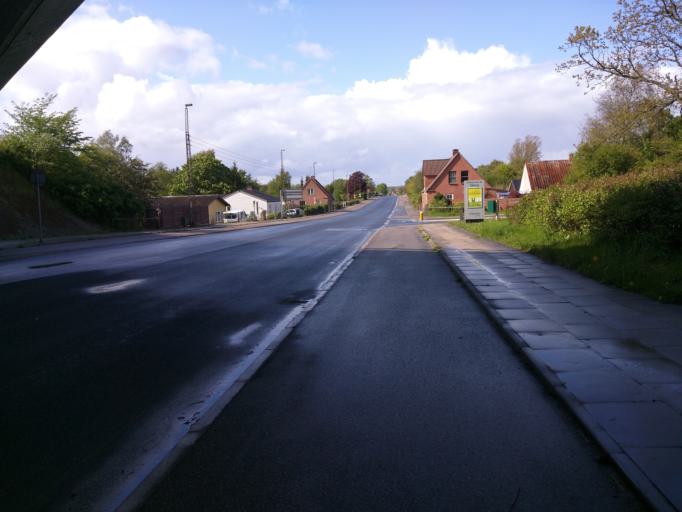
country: DK
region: Central Jutland
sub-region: Viborg Kommune
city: Viborg
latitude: 56.4208
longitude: 9.4045
